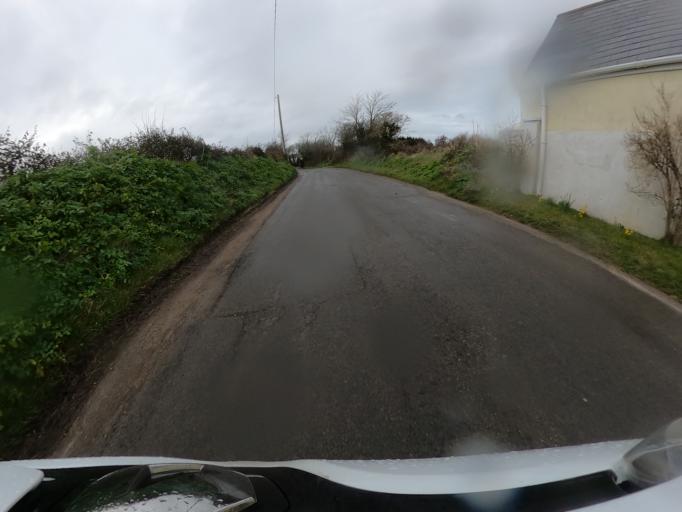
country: IM
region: Ramsey
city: Ramsey
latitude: 54.3738
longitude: -4.4510
